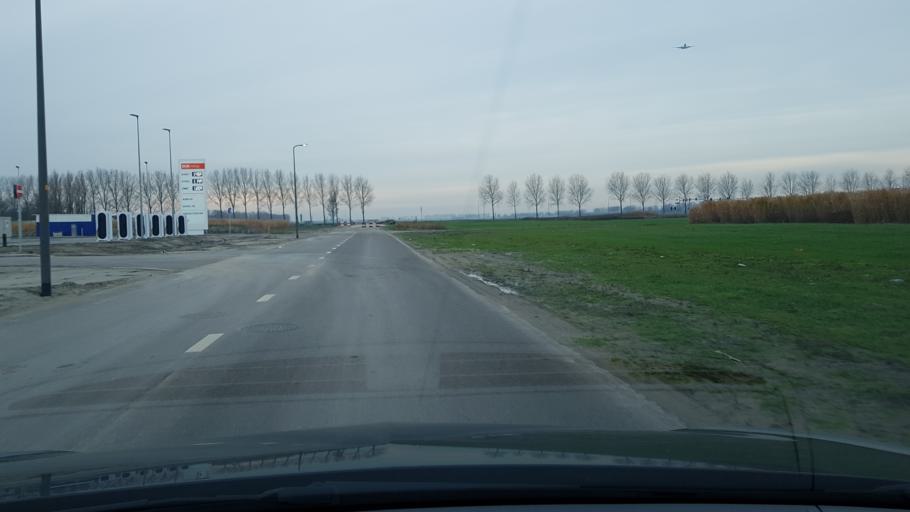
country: NL
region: North Holland
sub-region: Gemeente Haarlemmermeer
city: Hoofddorp
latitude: 52.2715
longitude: 4.6959
